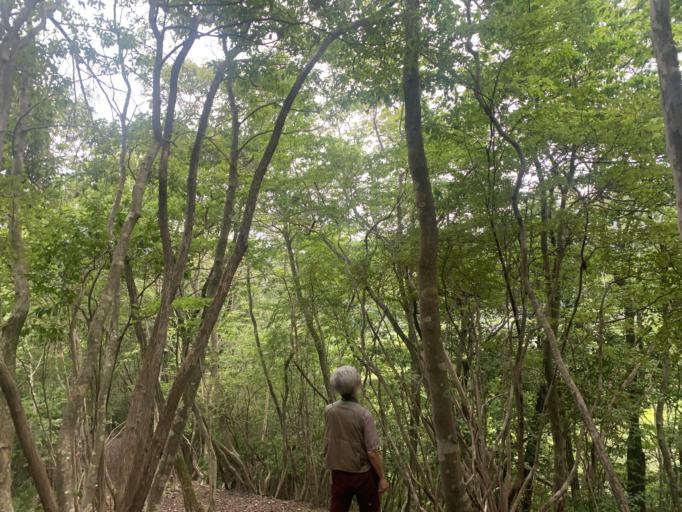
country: JP
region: Kyoto
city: Miyazu
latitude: 35.4478
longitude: 135.1631
